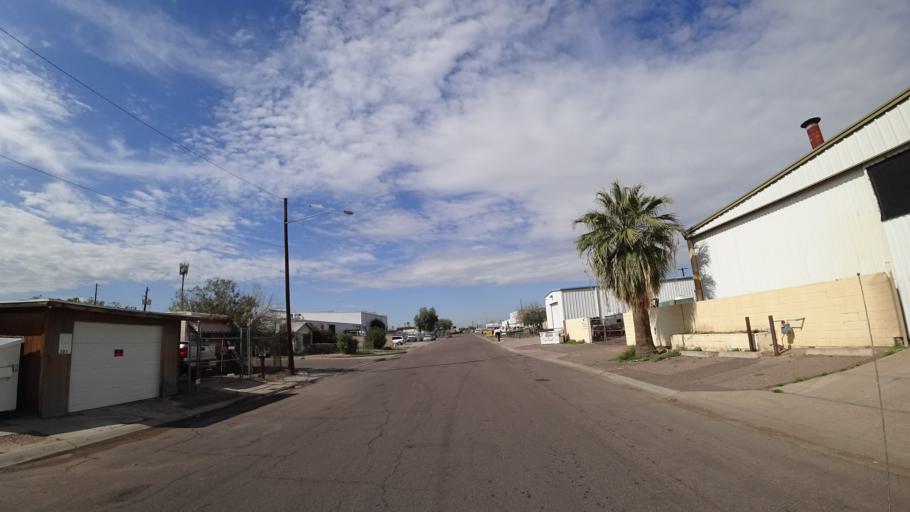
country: US
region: Arizona
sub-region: Maricopa County
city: Phoenix
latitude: 33.4175
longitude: -112.0694
